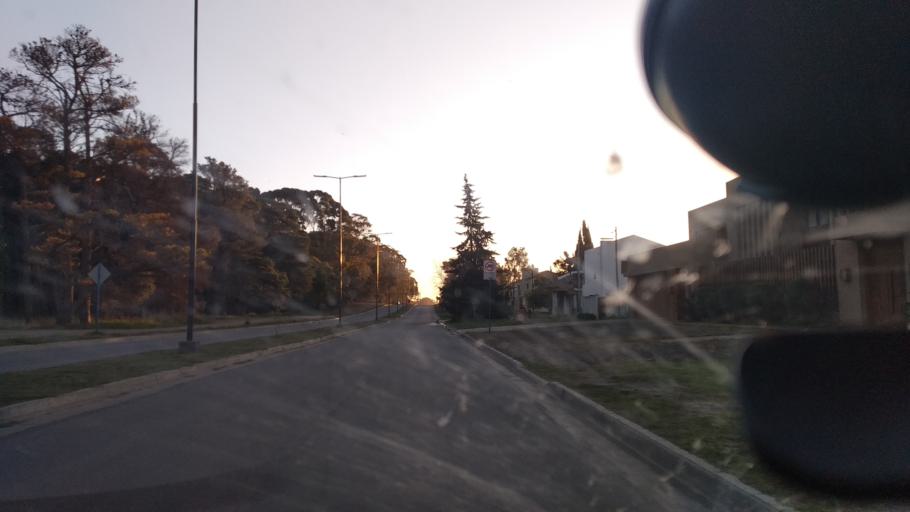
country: AR
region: Buenos Aires
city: Necochea
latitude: -38.5848
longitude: -58.7489
